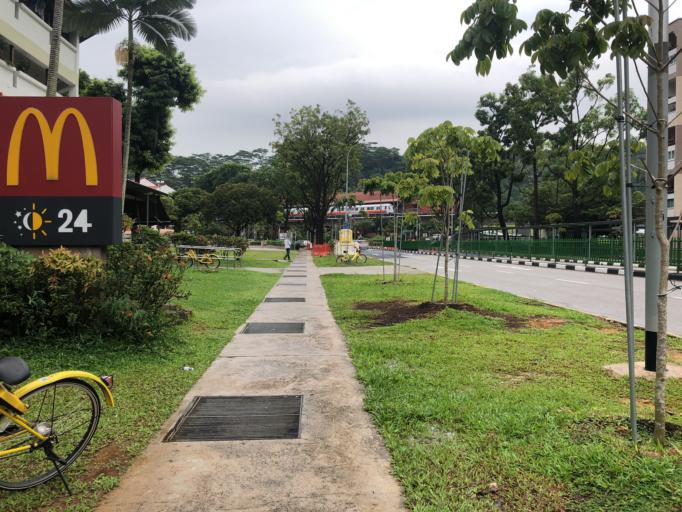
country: MY
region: Johor
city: Johor Bahru
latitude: 1.3574
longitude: 103.7506
